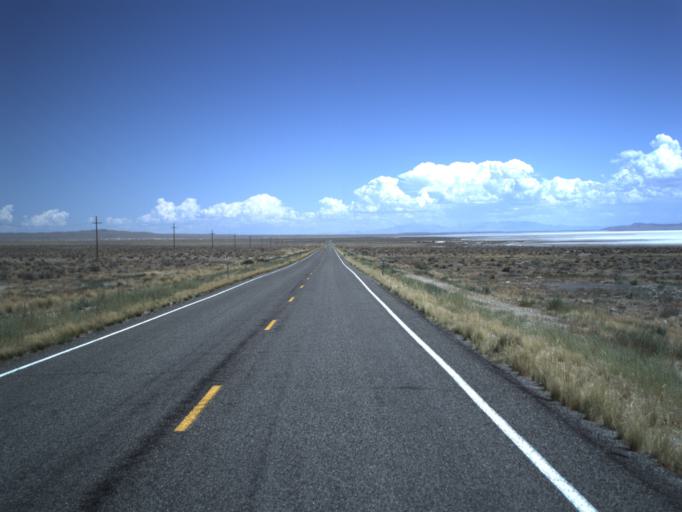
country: US
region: Utah
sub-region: Millard County
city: Delta
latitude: 39.0739
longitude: -113.2132
